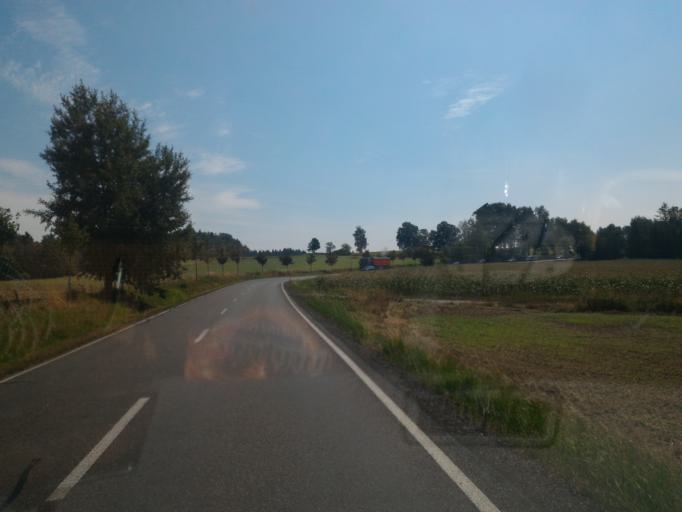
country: CZ
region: Pardubicky
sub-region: Okres Chrudim
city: Hlinsko
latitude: 49.7756
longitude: 15.8436
